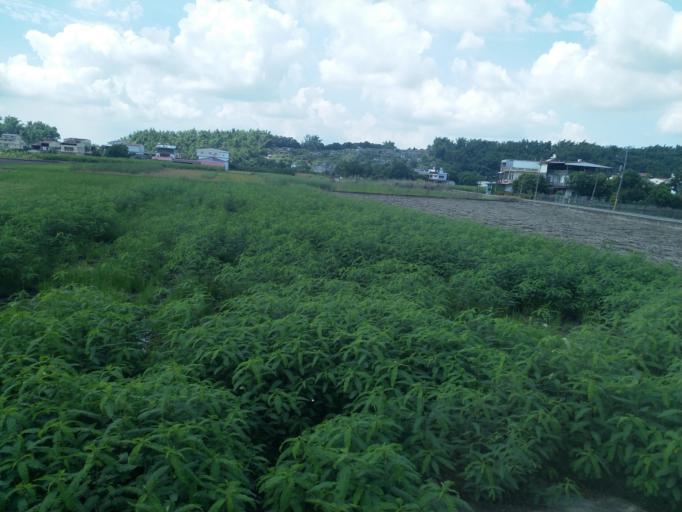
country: TW
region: Taiwan
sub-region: Pingtung
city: Pingtung
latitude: 22.8801
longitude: 120.5753
